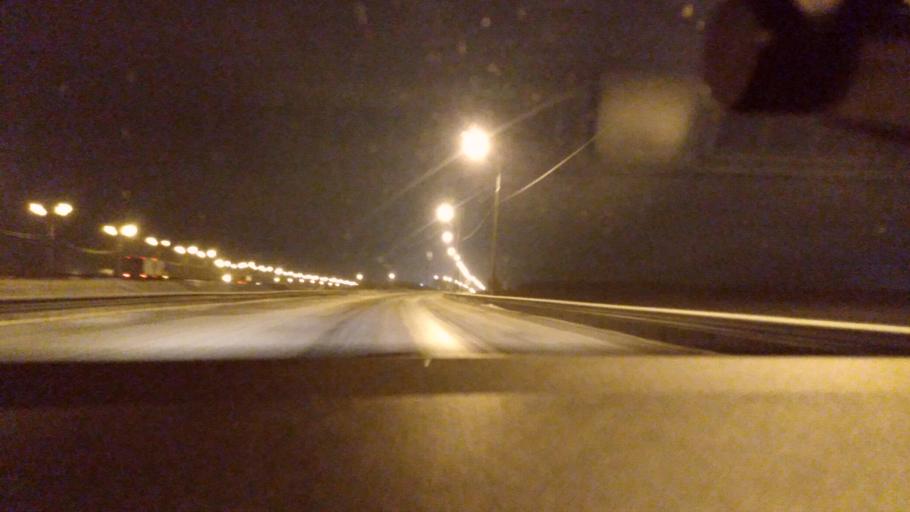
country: RU
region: Moskovskaya
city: Raduzhnyy
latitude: 55.1542
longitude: 38.6965
